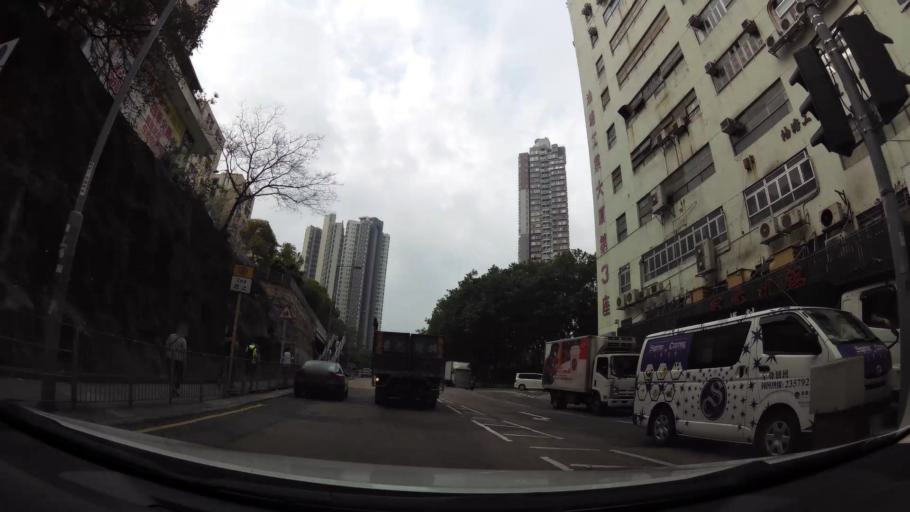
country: HK
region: Kowloon City
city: Kowloon
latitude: 22.2957
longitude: 114.2385
